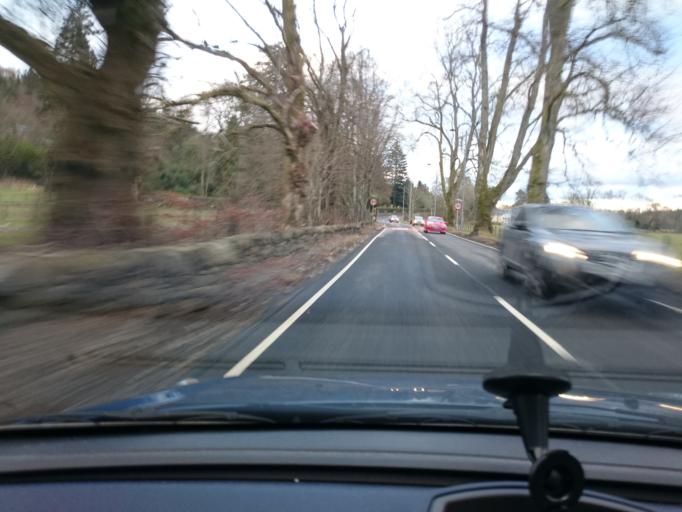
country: GB
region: Scotland
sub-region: Stirling
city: Callander
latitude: 56.2455
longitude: -4.2319
